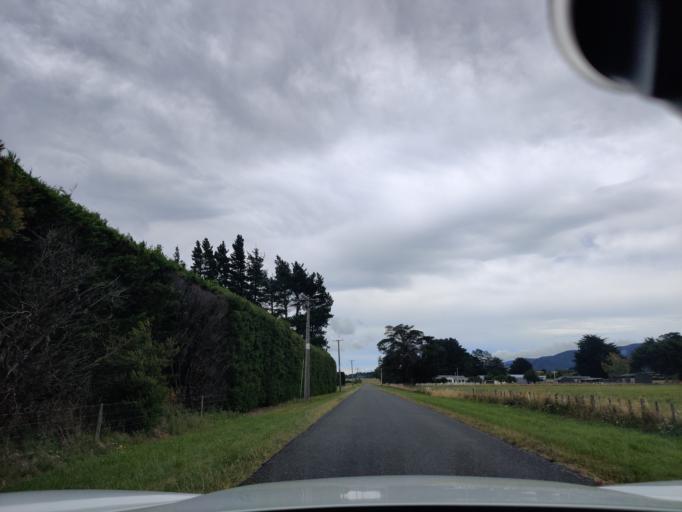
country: NZ
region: Wellington
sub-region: Masterton District
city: Masterton
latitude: -41.0254
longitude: 175.4557
